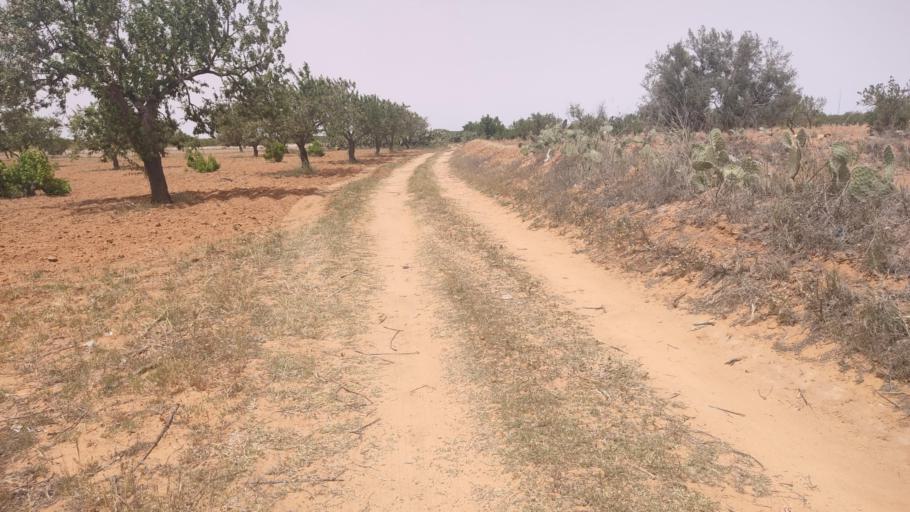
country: TN
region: Safaqis
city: Sfax
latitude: 34.8473
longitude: 10.5952
